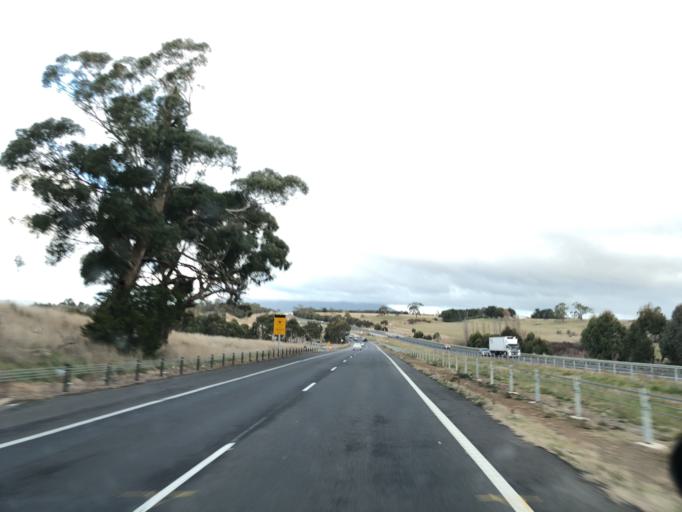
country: AU
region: Victoria
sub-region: Mount Alexander
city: Castlemaine
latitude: -37.2679
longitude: 144.4759
